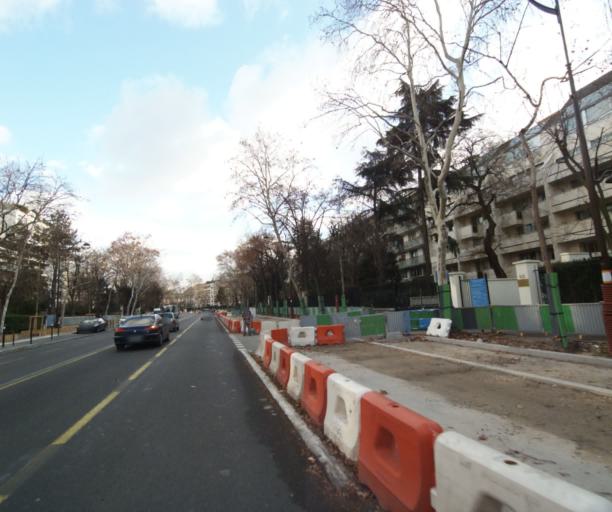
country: FR
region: Ile-de-France
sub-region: Departement des Hauts-de-Seine
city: Neuilly-sur-Seine
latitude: 48.8889
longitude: 2.2738
